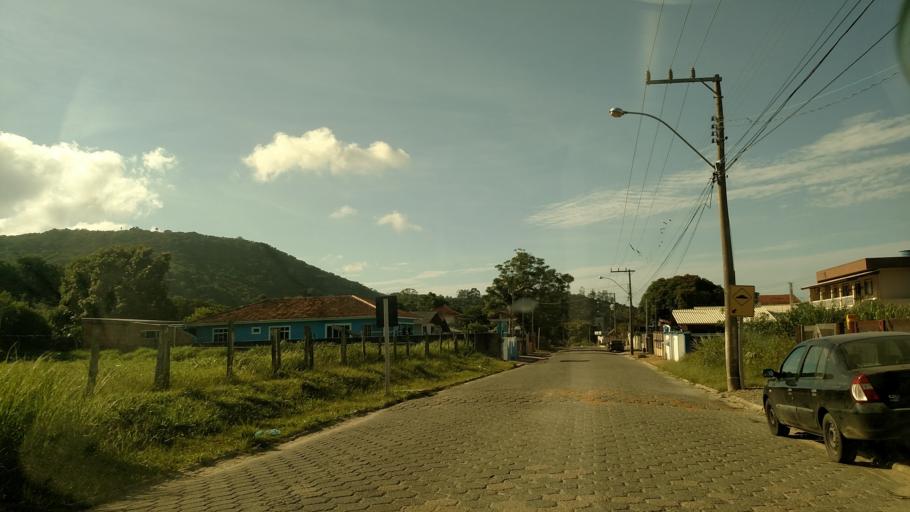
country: BR
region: Santa Catarina
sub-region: Porto Belo
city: Porto Belo
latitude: -27.1685
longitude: -48.5249
